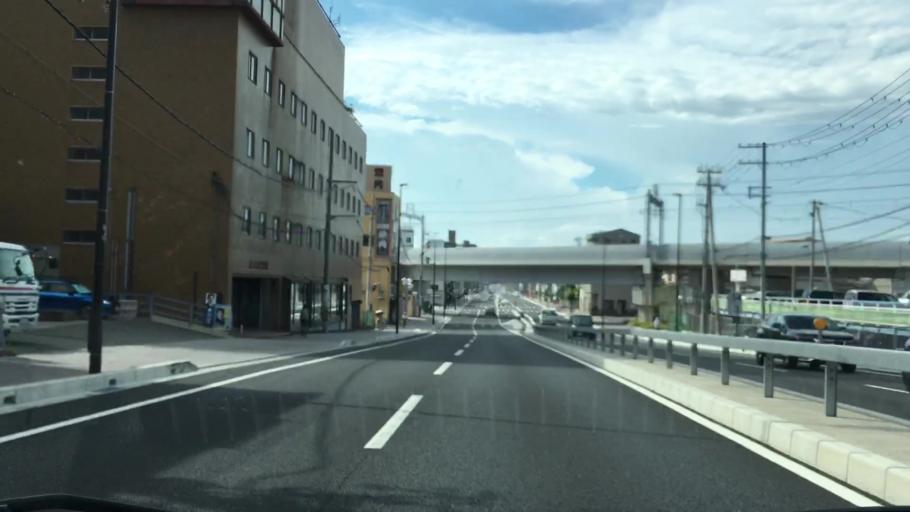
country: JP
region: Hyogo
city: Akashi
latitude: 34.6491
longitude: 134.9832
